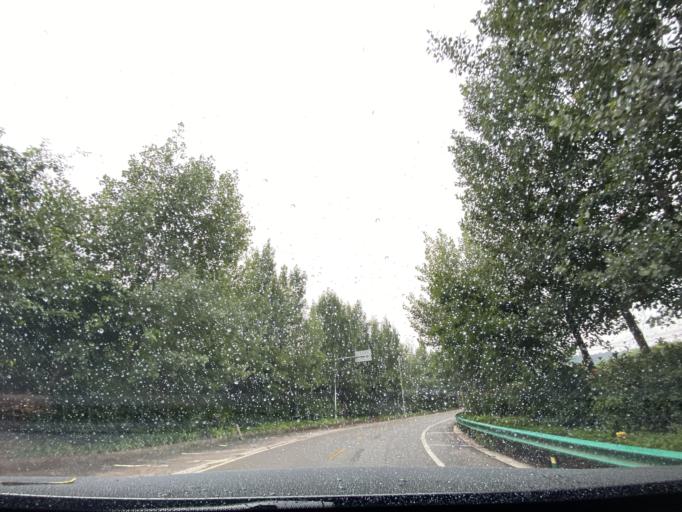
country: CN
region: Sichuan
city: Longquan
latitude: 30.6063
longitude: 104.4770
